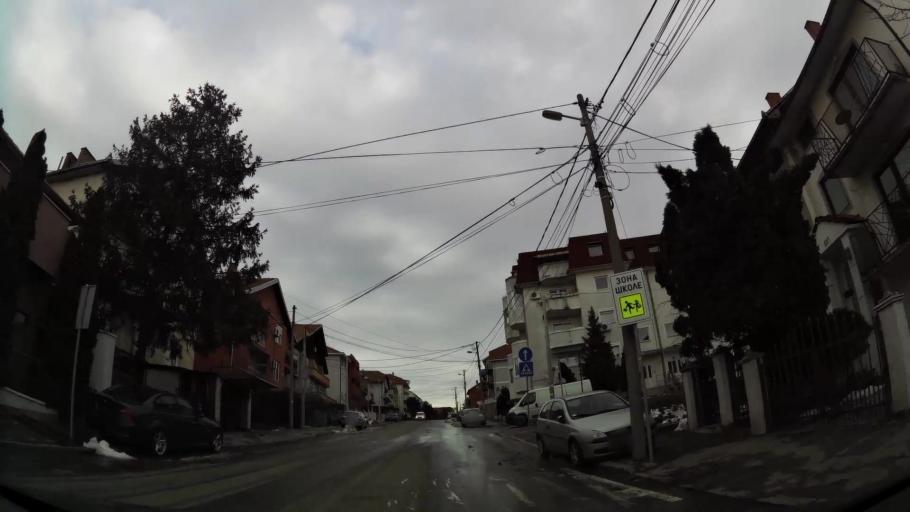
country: RS
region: Central Serbia
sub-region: Belgrade
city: Cukarica
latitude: 44.7544
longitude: 20.4066
